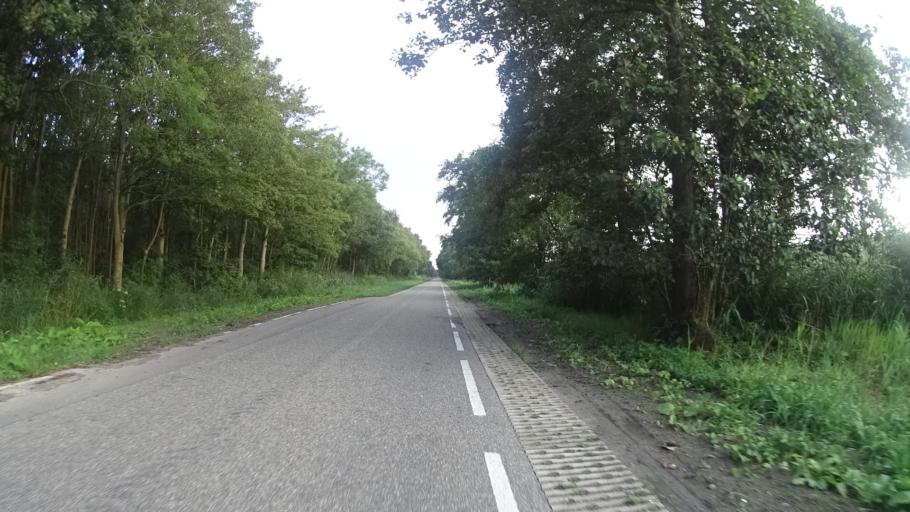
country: NL
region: North Holland
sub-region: Gemeente Hollands Kroon
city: Den Oever
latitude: 52.9097
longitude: 5.0592
